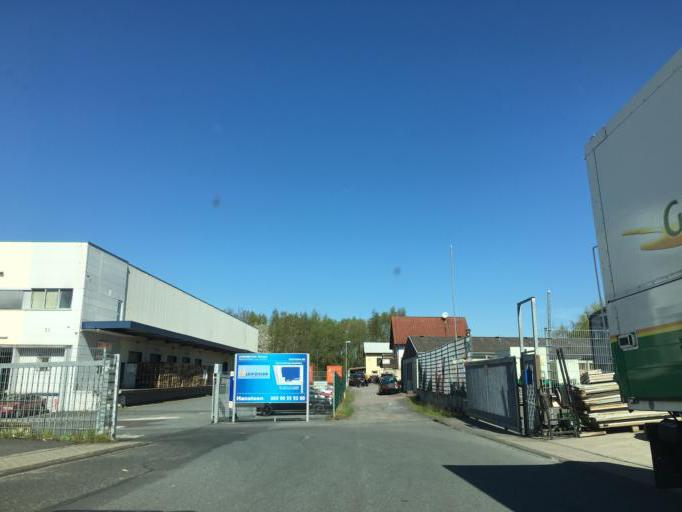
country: DE
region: Hesse
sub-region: Regierungsbezirk Darmstadt
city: Eppertshausen
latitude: 49.9895
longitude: 8.8625
